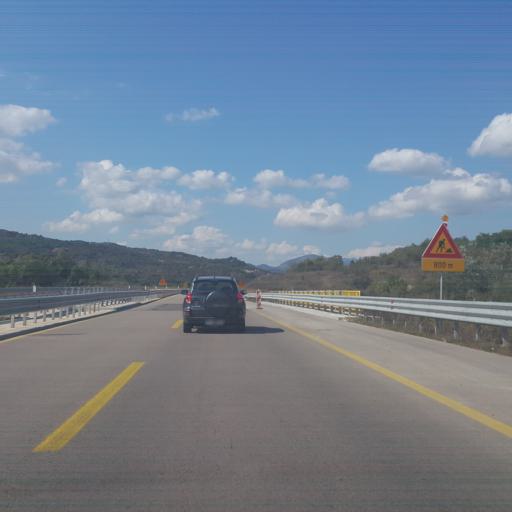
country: RS
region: Central Serbia
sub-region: Pirotski Okrug
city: Bela Palanka
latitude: 43.2478
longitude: 22.2763
